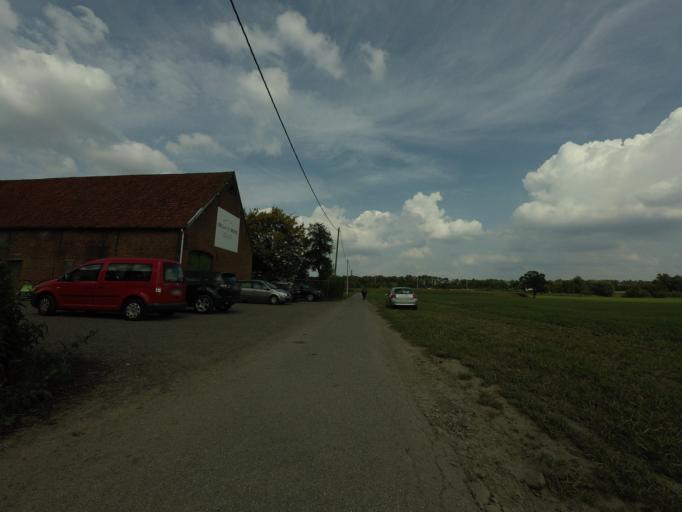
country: BE
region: Flanders
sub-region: Provincie Antwerpen
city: Edegem
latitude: 51.1493
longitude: 4.4176
